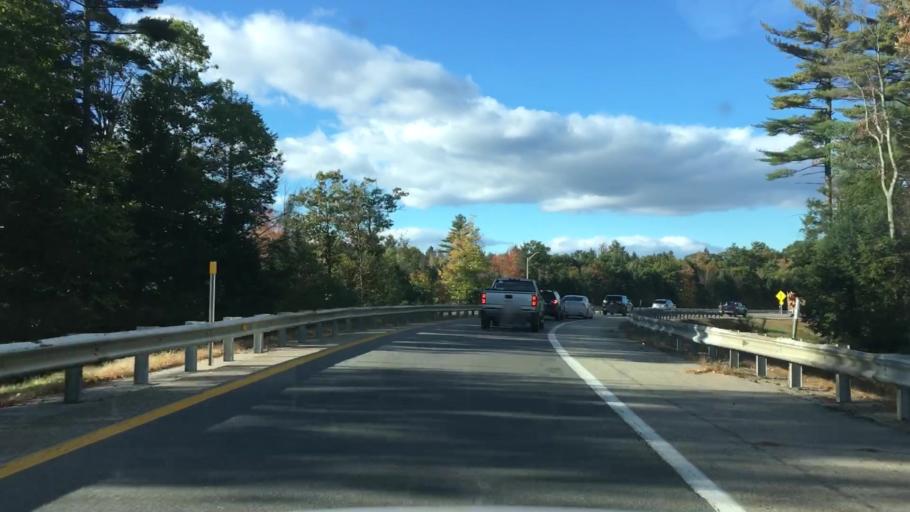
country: US
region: Maine
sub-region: York County
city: Wells Beach Station
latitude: 43.3262
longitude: -70.6051
